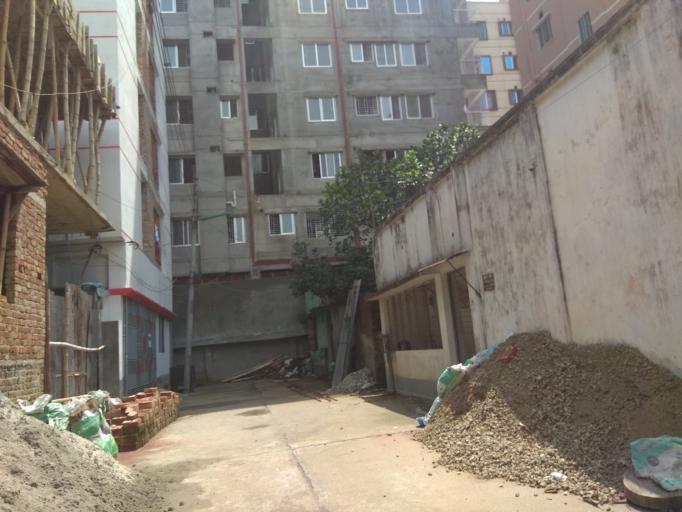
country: BD
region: Dhaka
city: Azimpur
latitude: 23.8064
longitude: 90.3551
